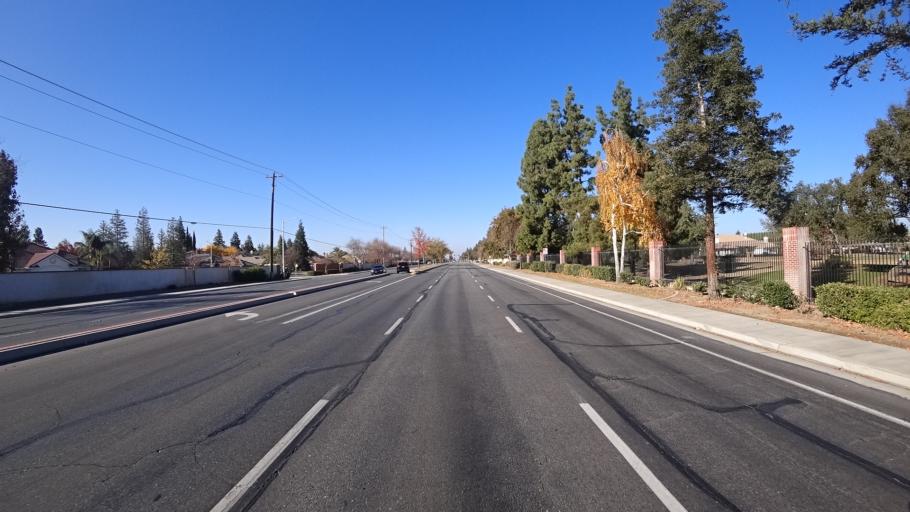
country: US
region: California
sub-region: Kern County
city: Greenacres
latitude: 35.3253
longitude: -119.1153
